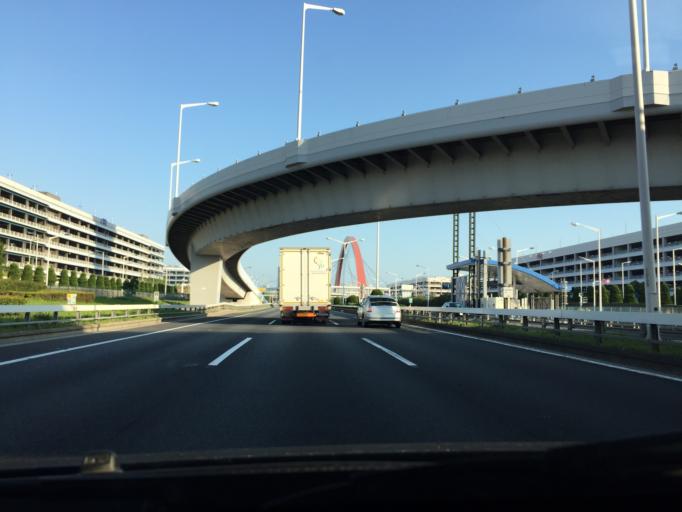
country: JP
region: Kanagawa
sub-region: Kawasaki-shi
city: Kawasaki
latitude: 35.5530
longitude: 139.7843
